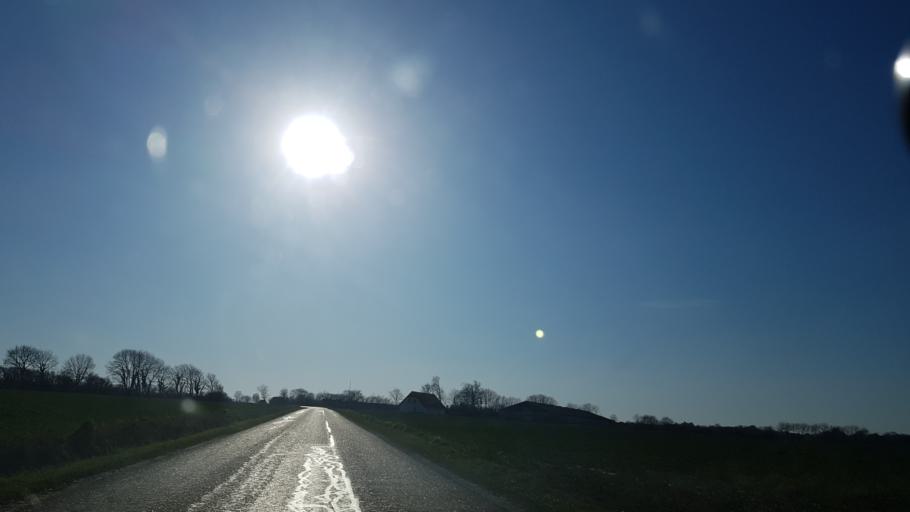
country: DK
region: South Denmark
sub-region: Vejen Kommune
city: Rodding
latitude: 55.3911
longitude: 9.0647
